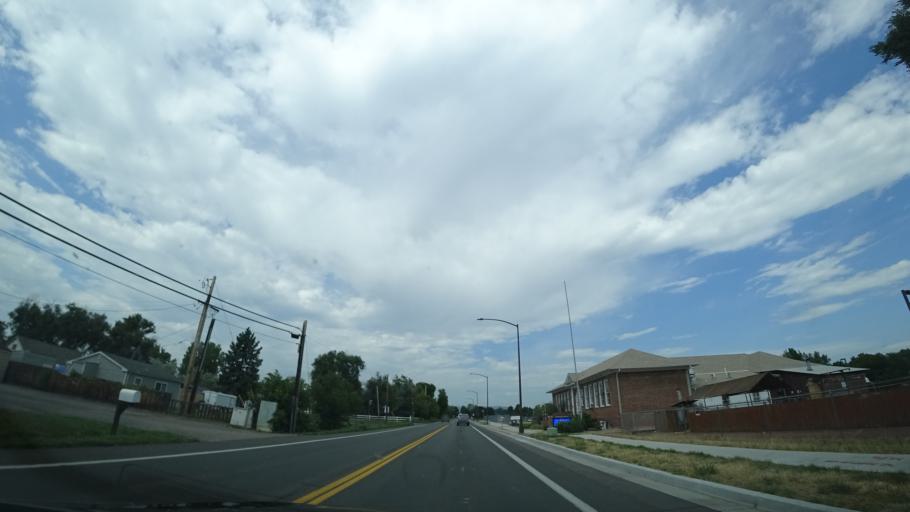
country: US
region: Colorado
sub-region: Jefferson County
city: Lakewood
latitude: 39.7186
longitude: -105.0665
